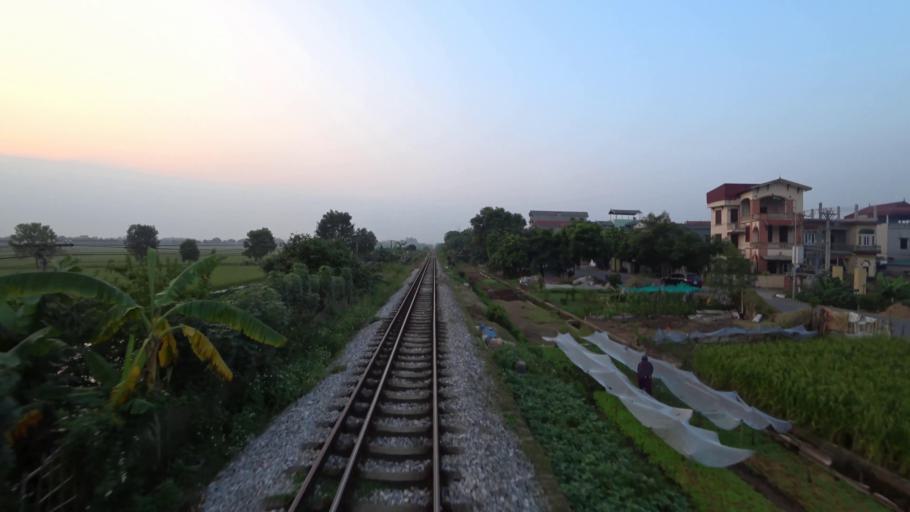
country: VN
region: Ha Noi
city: Dong Anh
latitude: 21.1282
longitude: 105.8783
